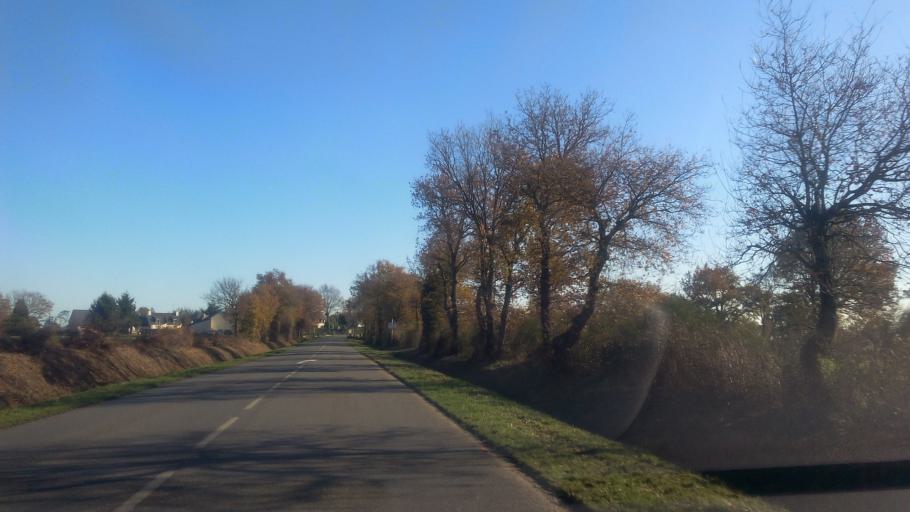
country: FR
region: Brittany
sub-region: Departement du Morbihan
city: Saint-Vincent-sur-Oust
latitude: 47.7034
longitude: -2.1527
